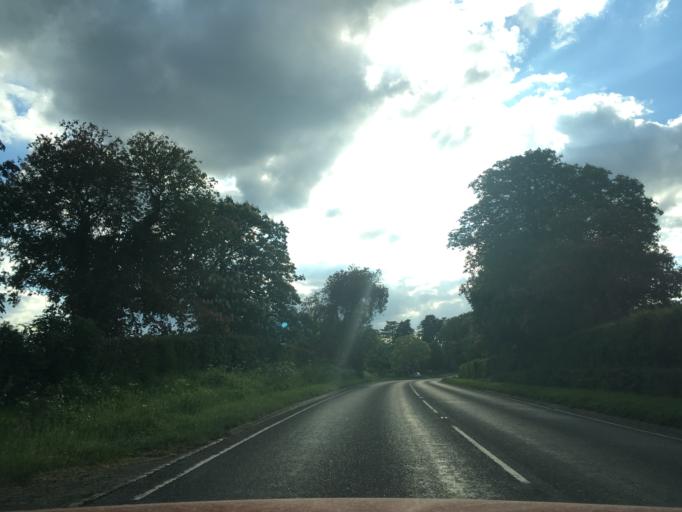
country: GB
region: England
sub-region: Worcestershire
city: Fernhill Heath
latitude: 52.1823
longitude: -2.1455
